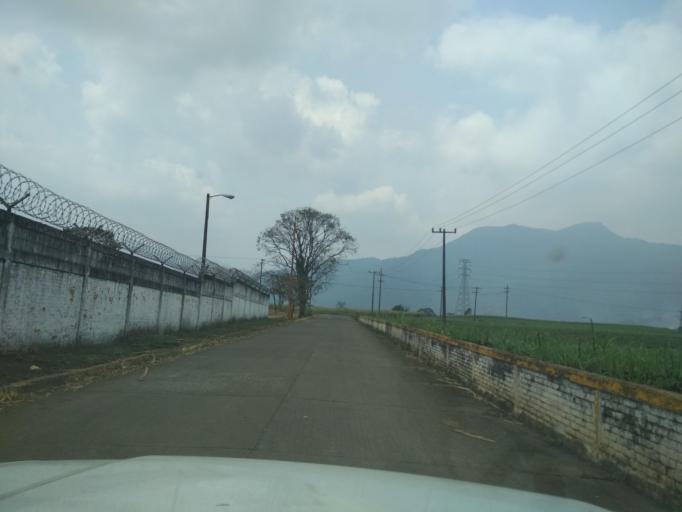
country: MX
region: Veracruz
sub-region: Cordoba
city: San Jose de Tapia
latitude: 18.8362
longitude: -96.9761
